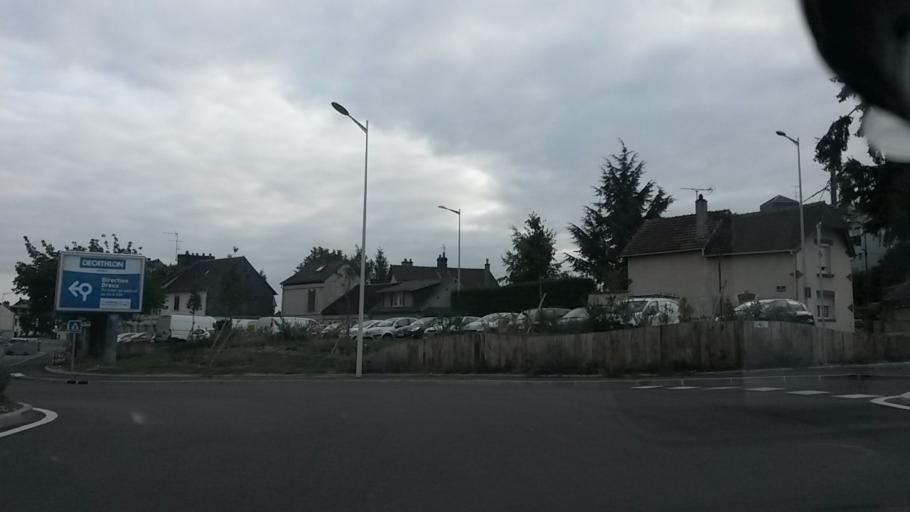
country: FR
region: Haute-Normandie
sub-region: Departement de l'Eure
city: Evreux
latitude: 49.0346
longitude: 1.1559
